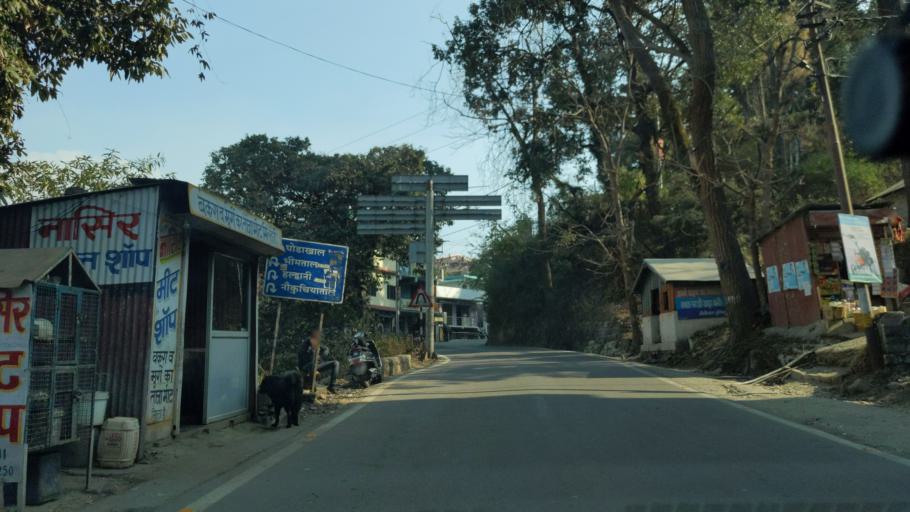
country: IN
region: Uttarakhand
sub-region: Naini Tal
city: Bhowali
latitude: 29.3826
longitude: 79.5206
